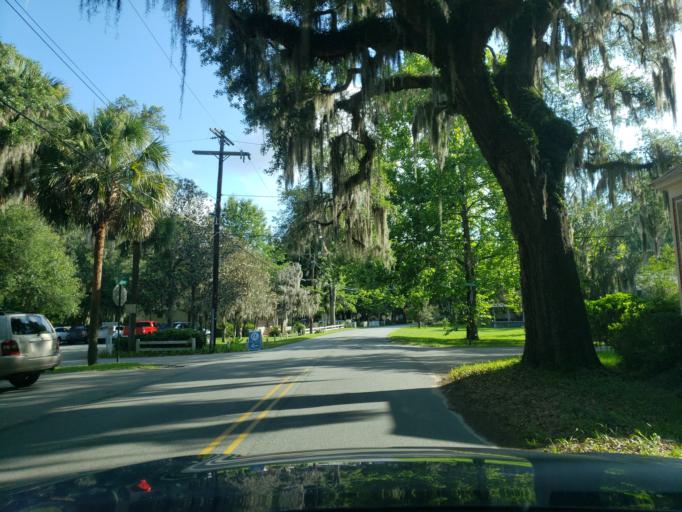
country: US
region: Georgia
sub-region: Chatham County
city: Isle of Hope
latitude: 31.9819
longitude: -81.0589
